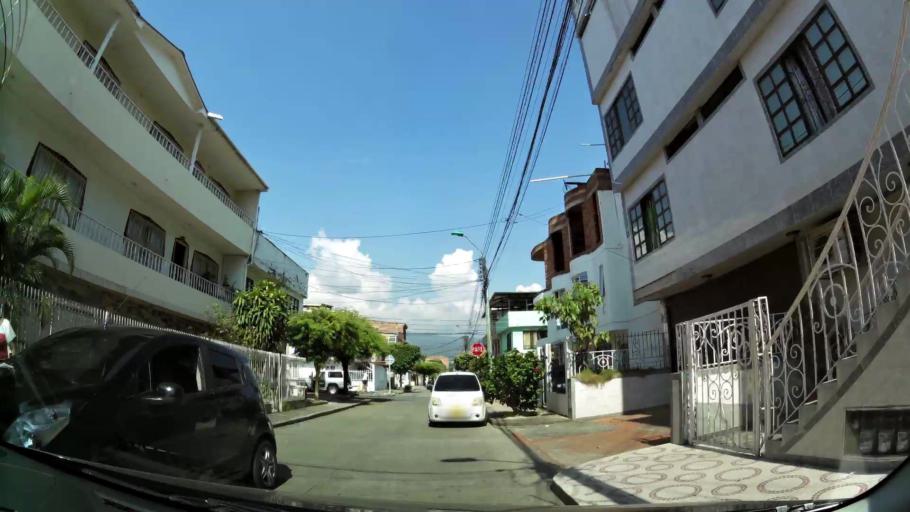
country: CO
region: Valle del Cauca
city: Cali
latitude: 3.4051
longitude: -76.5251
